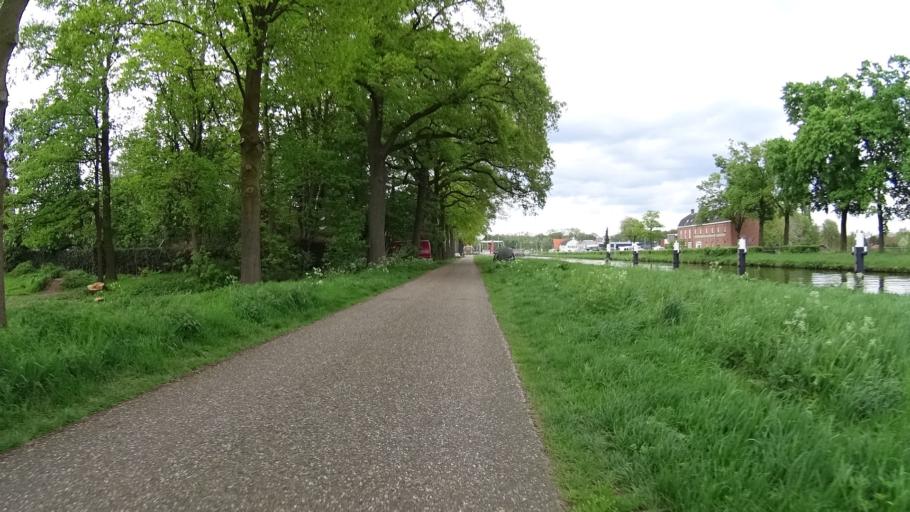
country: NL
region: North Brabant
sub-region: Gemeente Laarbeek
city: Aarle-Rixtel
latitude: 51.5263
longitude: 5.6435
